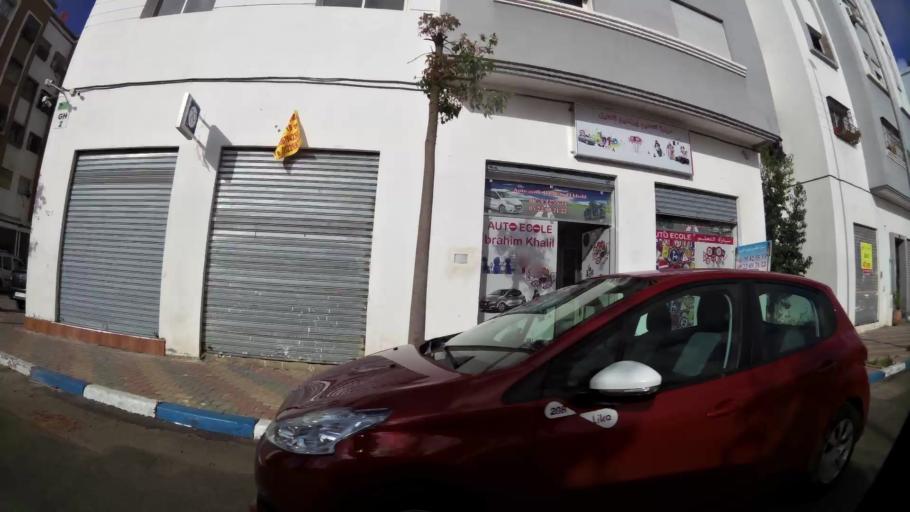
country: MA
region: Grand Casablanca
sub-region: Casablanca
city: Casablanca
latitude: 33.5498
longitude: -7.7009
